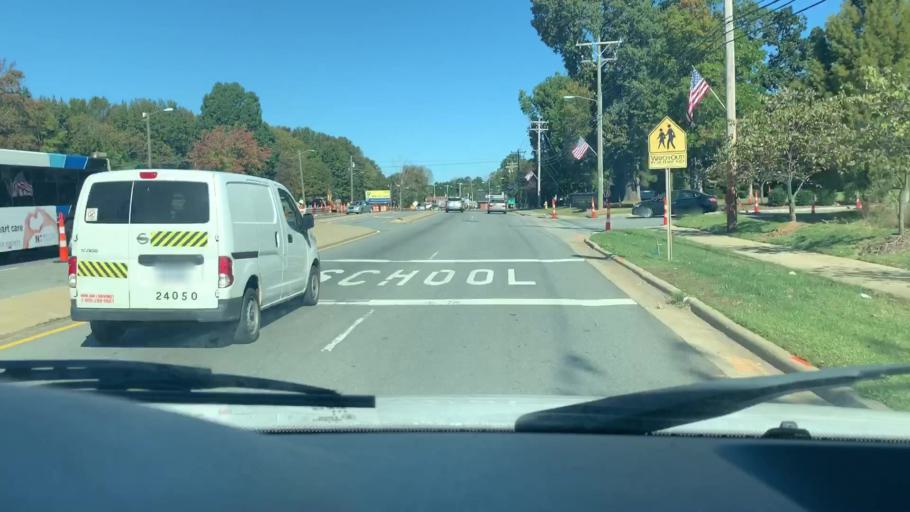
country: US
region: North Carolina
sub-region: Mecklenburg County
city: Charlotte
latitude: 35.2932
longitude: -80.7969
